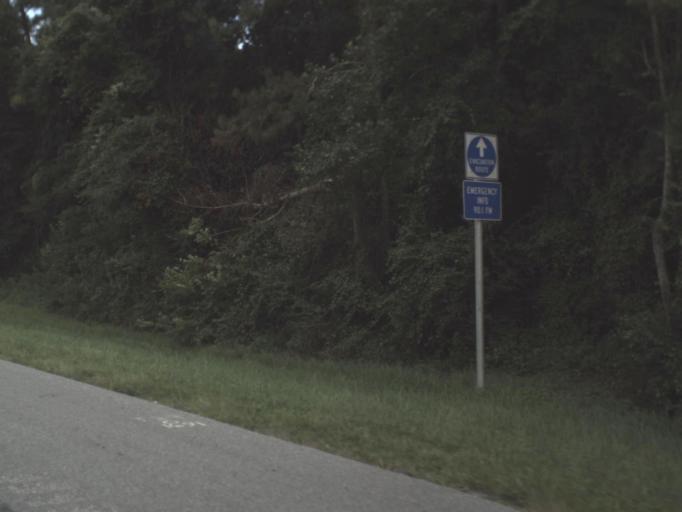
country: US
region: Florida
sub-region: Hernando County
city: Hill 'n Dale
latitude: 28.4391
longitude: -82.2808
